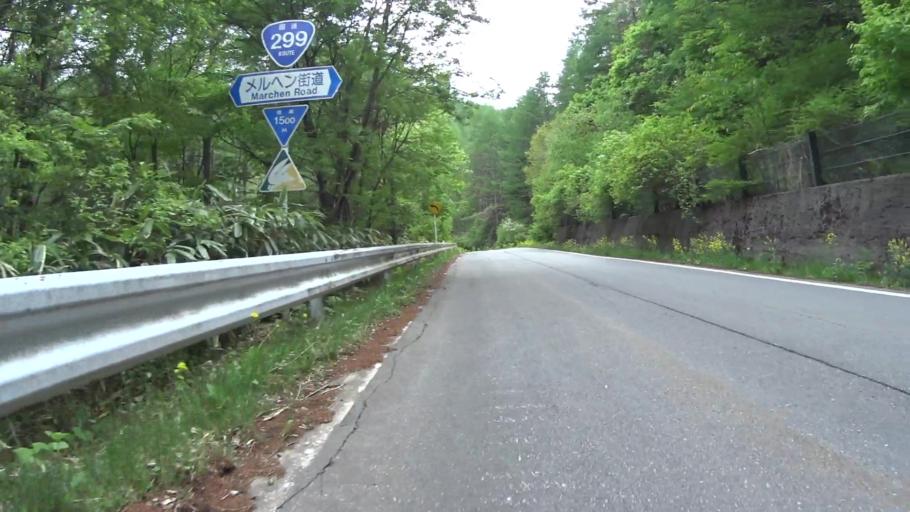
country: JP
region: Nagano
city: Saku
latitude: 36.0916
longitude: 138.3864
